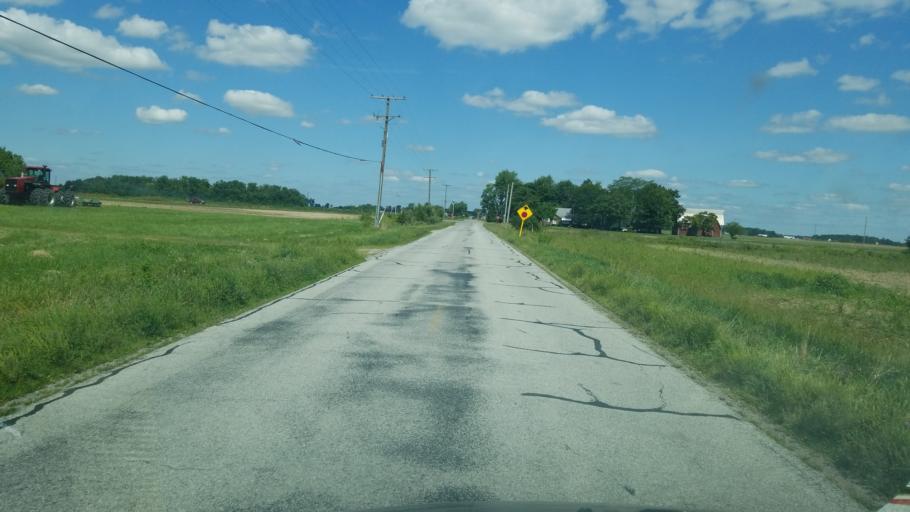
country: US
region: Ohio
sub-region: Fulton County
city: Swanton
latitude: 41.5863
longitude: -83.9407
